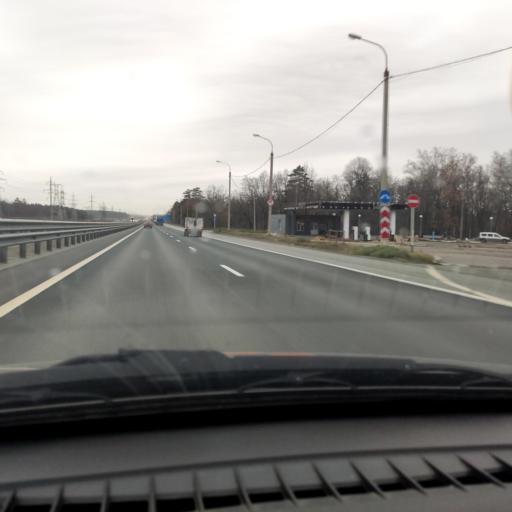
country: RU
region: Samara
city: Povolzhskiy
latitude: 53.5159
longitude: 49.6956
